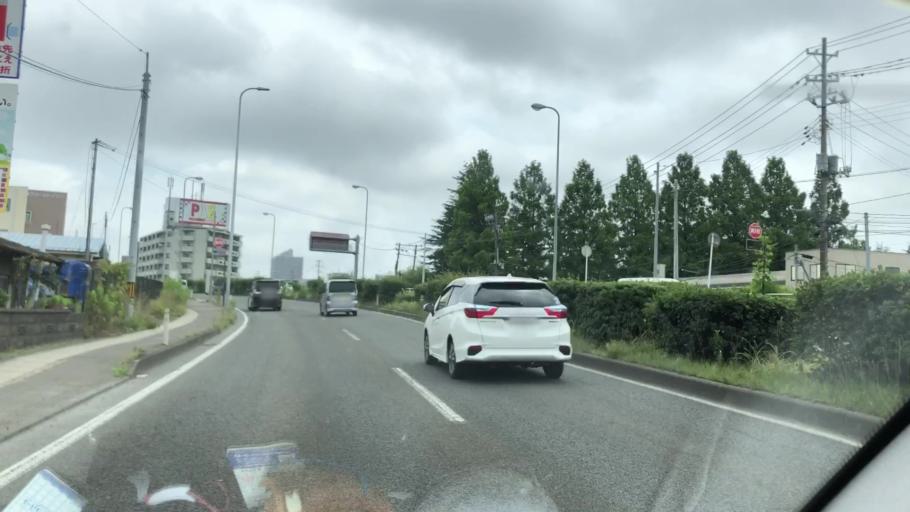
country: JP
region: Miyagi
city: Rifu
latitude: 38.2707
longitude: 140.9552
